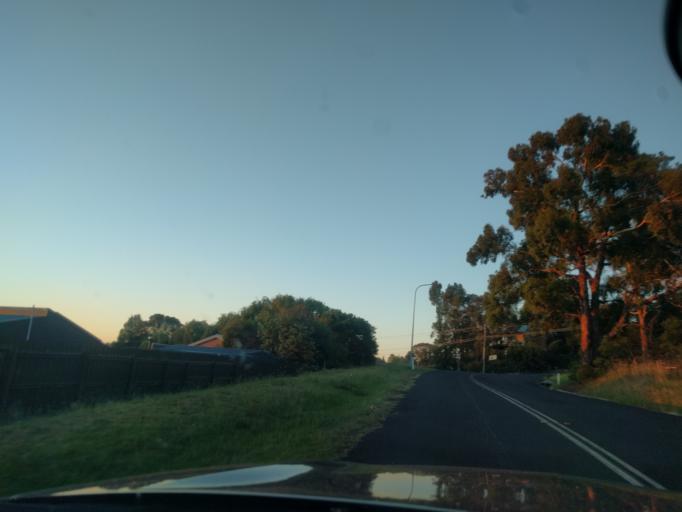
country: AU
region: New South Wales
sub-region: Armidale Dumaresq
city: Armidale
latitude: -30.5008
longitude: 151.6616
